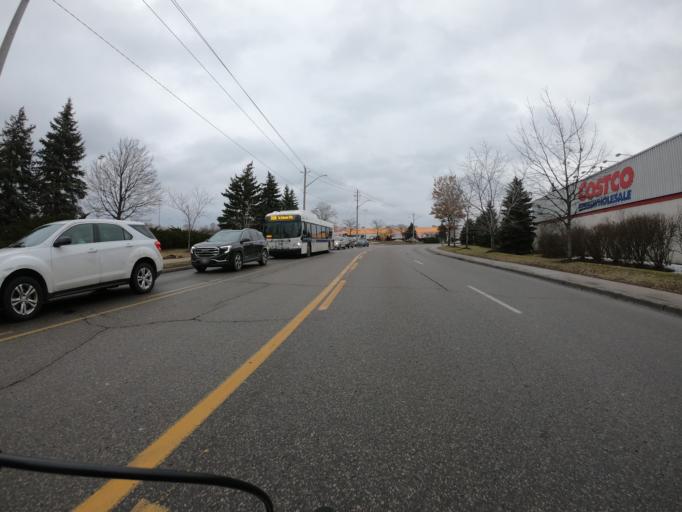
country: CA
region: Ontario
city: Cambridge
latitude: 43.4078
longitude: -80.3910
